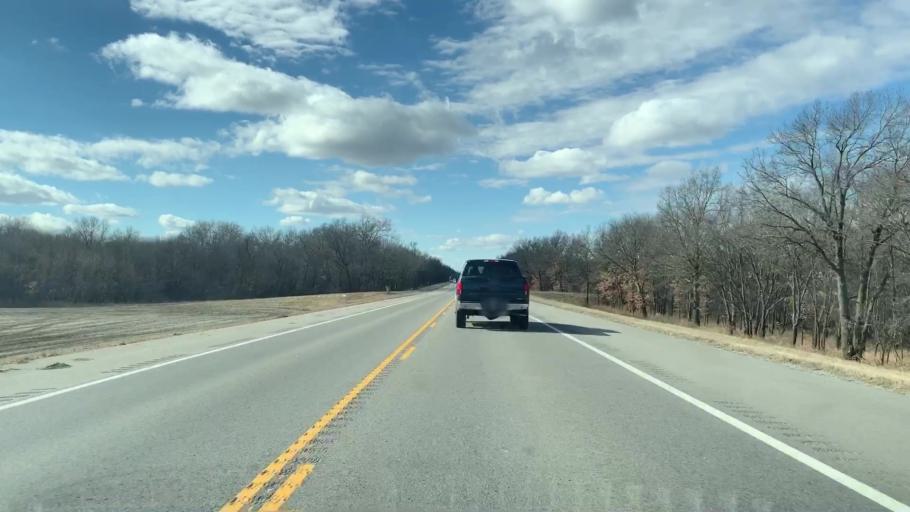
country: US
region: Kansas
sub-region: Cherokee County
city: Columbus
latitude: 37.3401
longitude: -94.9662
